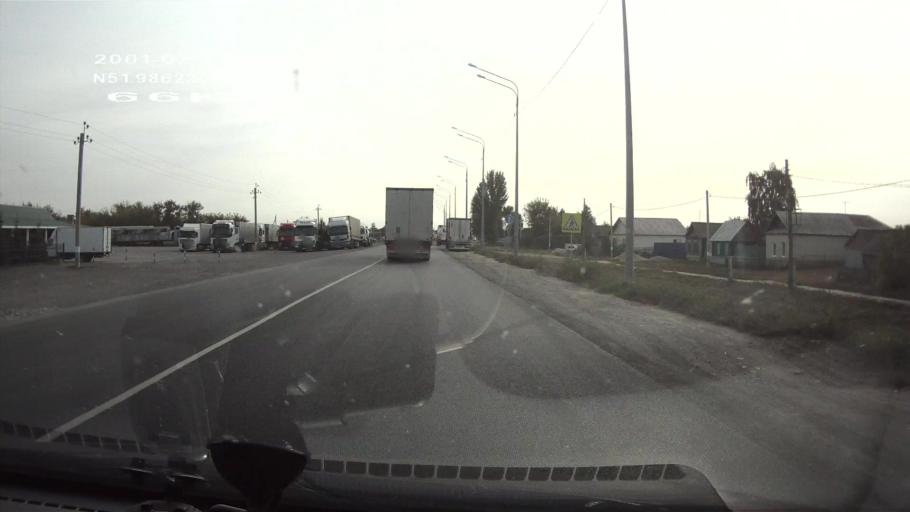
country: RU
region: Saratov
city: Sinodskoye
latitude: 51.9859
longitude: 46.6636
